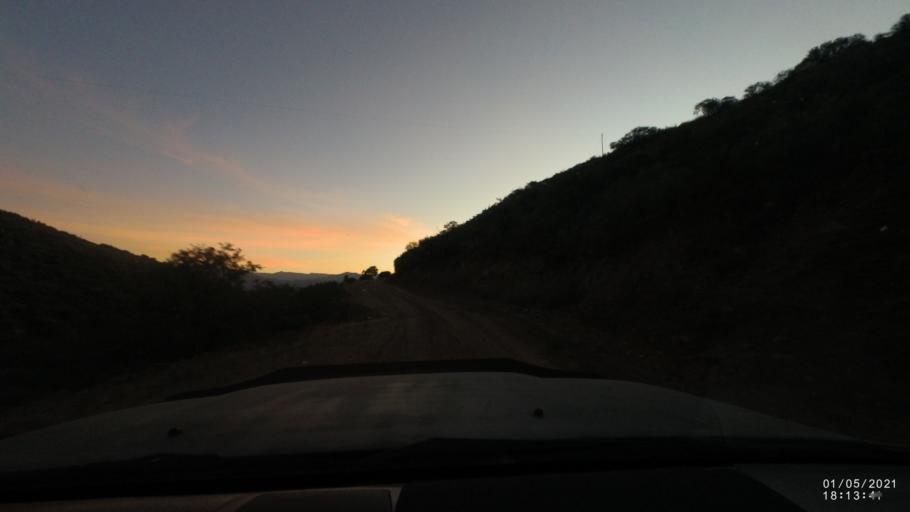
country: BO
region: Cochabamba
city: Capinota
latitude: -17.6747
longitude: -66.2079
